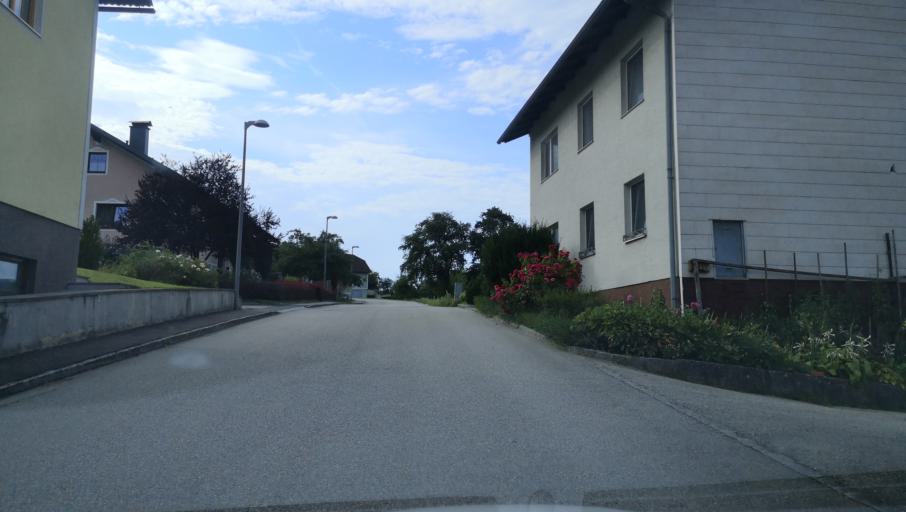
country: AT
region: Lower Austria
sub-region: Politischer Bezirk Amstetten
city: Zeillern
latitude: 48.1580
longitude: 14.8216
